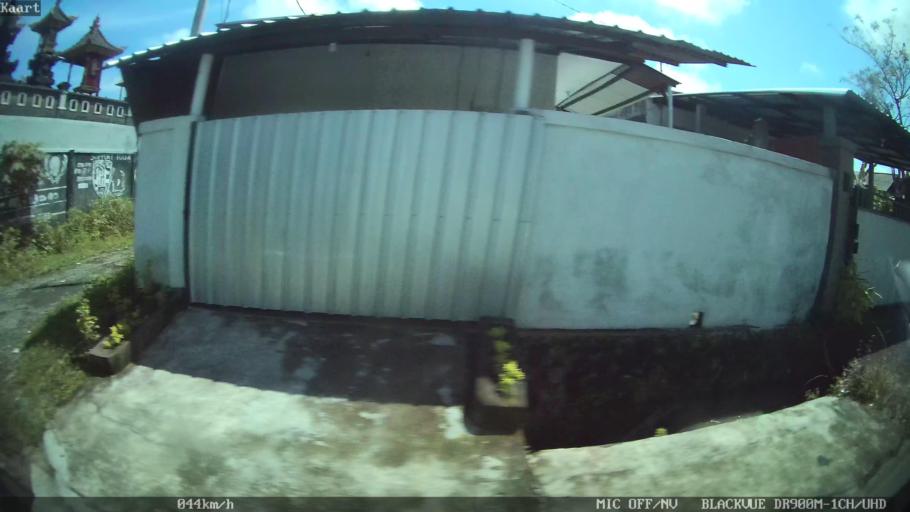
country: ID
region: Bali
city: Banjar Kelodan
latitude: -8.5285
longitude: 115.3356
